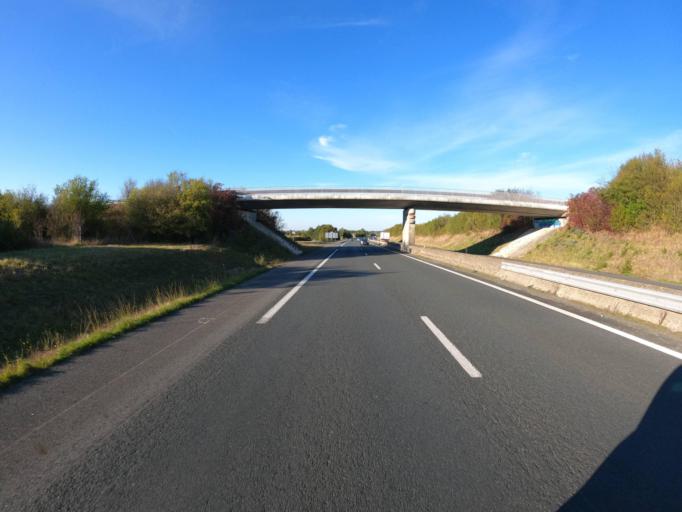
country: FR
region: Pays de la Loire
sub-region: Departement de Maine-et-Loire
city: Mazieres-en-Mauges
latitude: 47.0740
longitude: -0.8263
